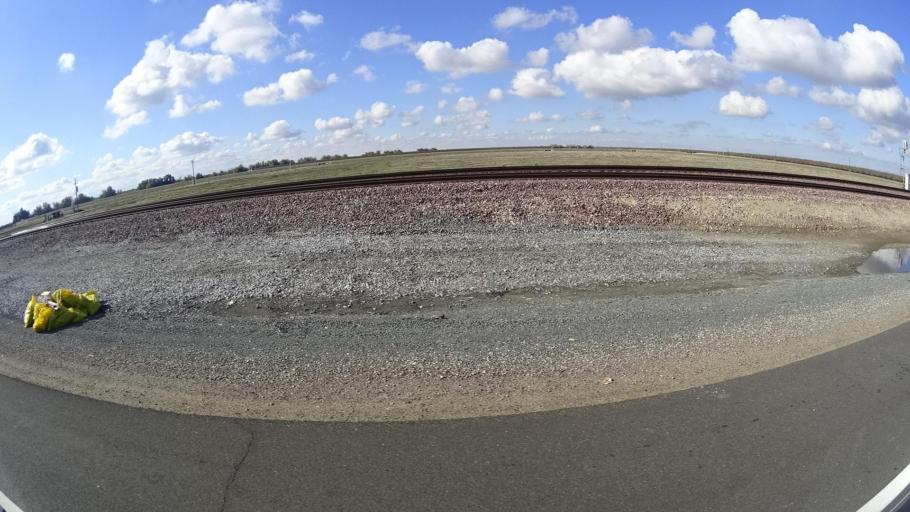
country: US
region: California
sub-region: Kern County
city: Wasco
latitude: 35.6714
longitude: -119.3299
